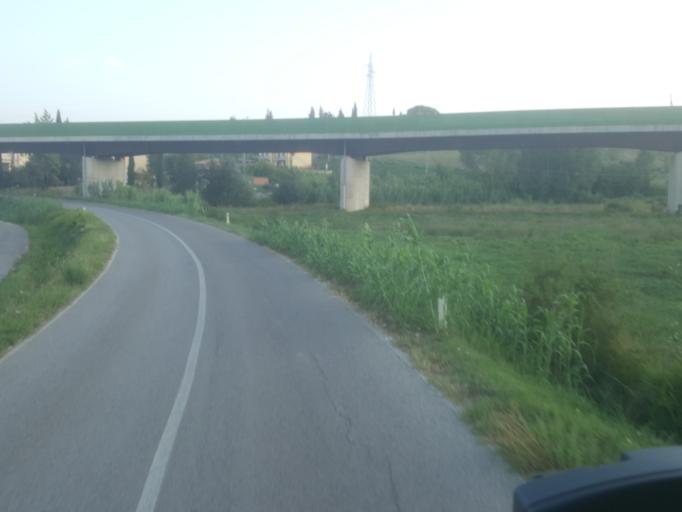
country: IT
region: Tuscany
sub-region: Province of Florence
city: Certaldo
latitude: 43.5339
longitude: 11.0337
